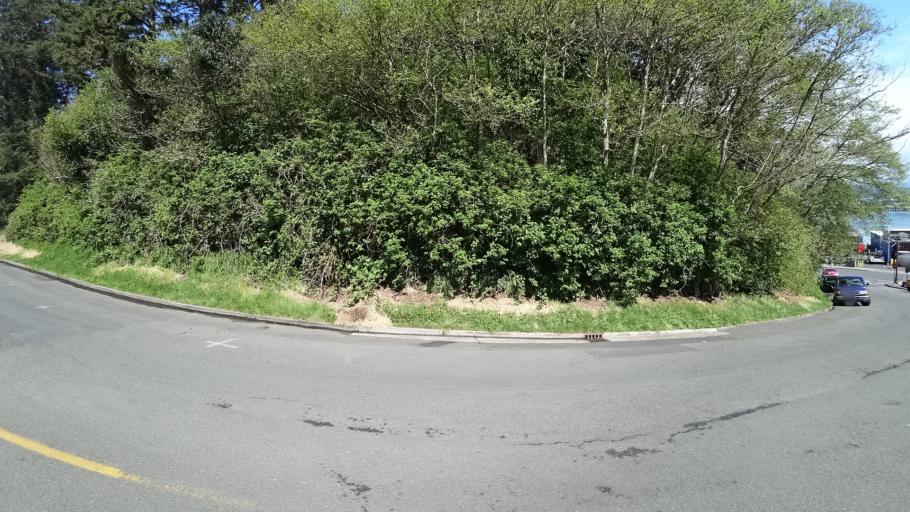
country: US
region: Oregon
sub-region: Lincoln County
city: Newport
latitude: 44.6298
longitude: -124.0554
